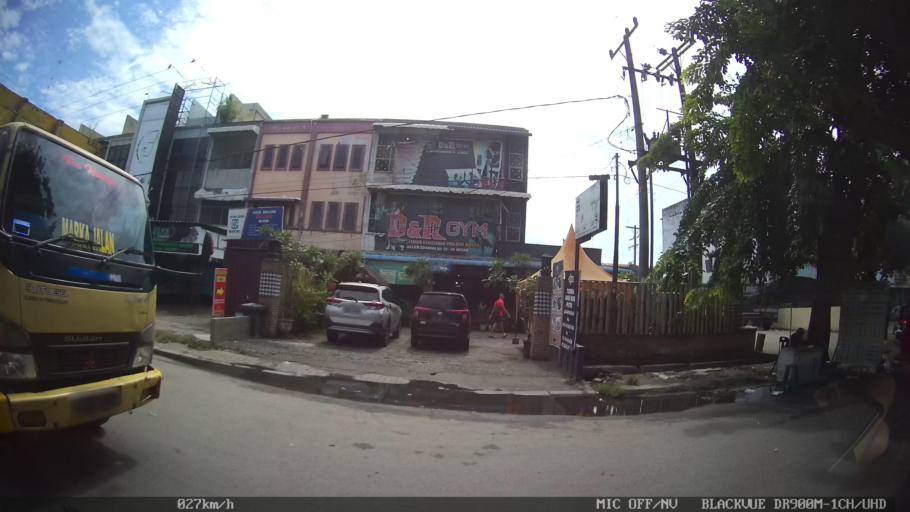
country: ID
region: North Sumatra
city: Medan
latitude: 3.6050
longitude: 98.7070
